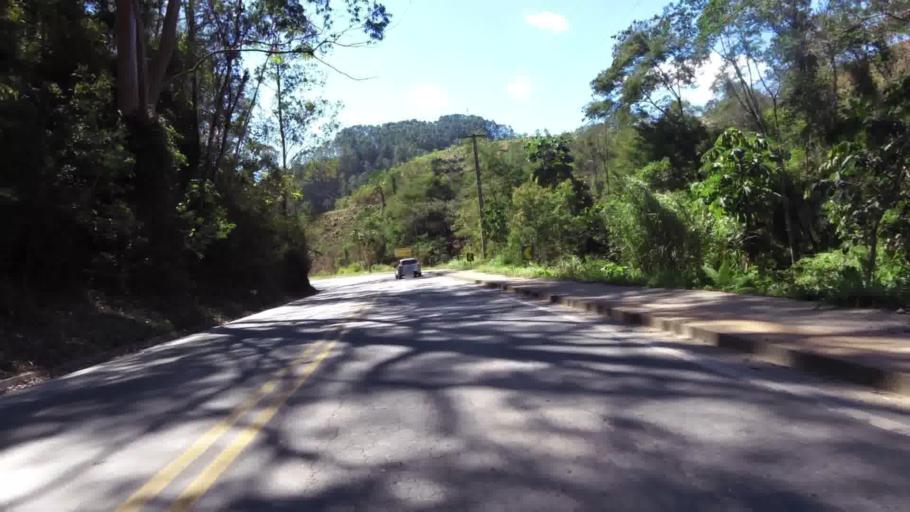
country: BR
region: Espirito Santo
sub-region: Vargem Alta
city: Vargem Alta
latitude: -20.6787
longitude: -41.0143
